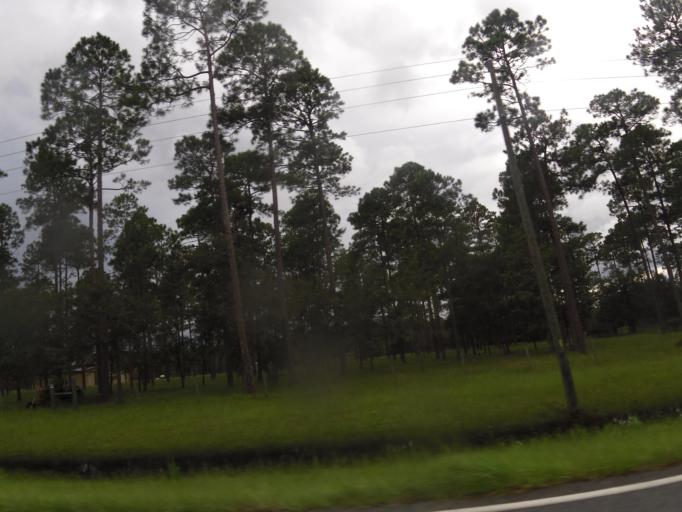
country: US
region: Florida
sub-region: Baker County
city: Macclenny
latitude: 30.4780
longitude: -82.1986
